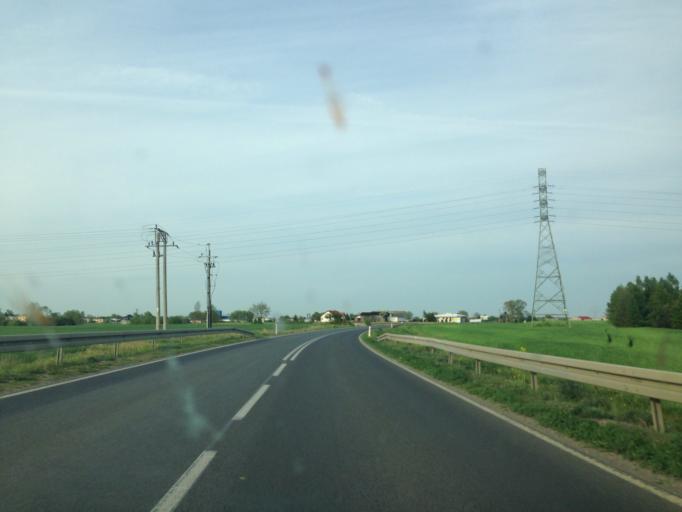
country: PL
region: Kujawsko-Pomorskie
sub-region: Powiat wabrzeski
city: Wabrzezno
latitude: 53.2662
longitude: 18.9607
